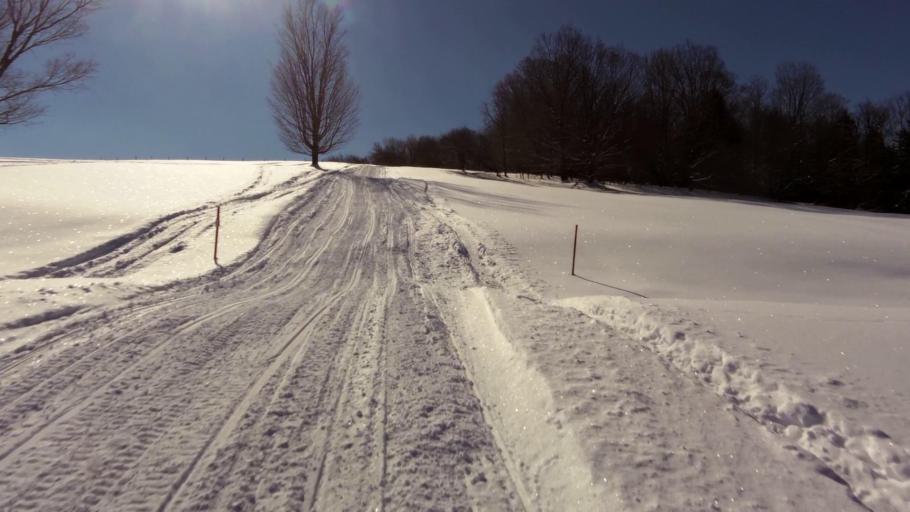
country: US
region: New York
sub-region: Chautauqua County
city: Fredonia
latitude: 42.3556
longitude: -79.1887
